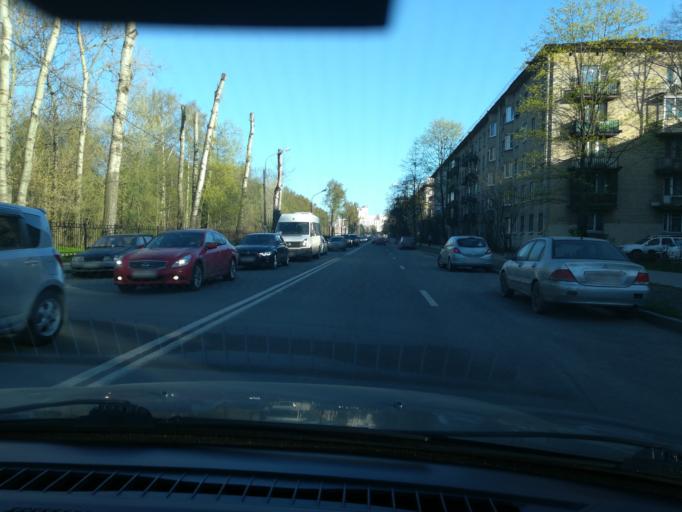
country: RU
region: St.-Petersburg
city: Vasyl'evsky Ostrov
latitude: 59.9432
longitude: 30.2392
